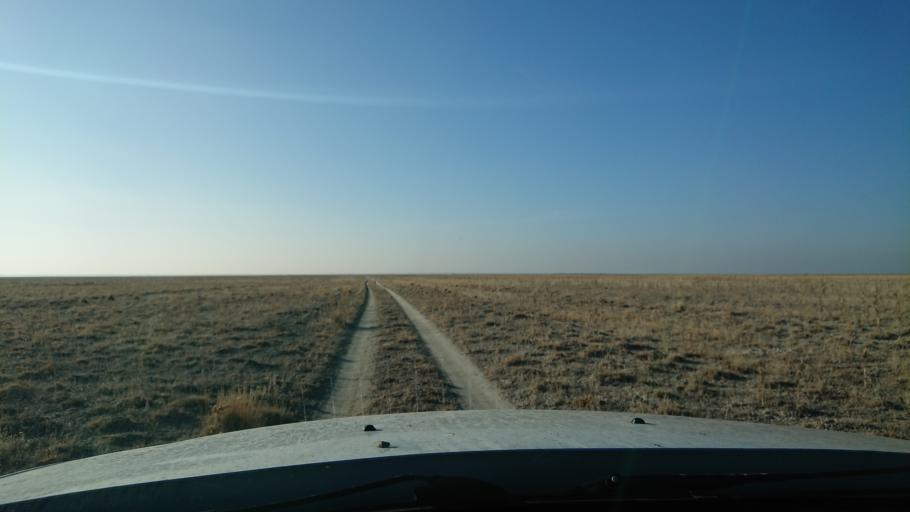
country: TR
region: Aksaray
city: Sultanhani
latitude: 38.3711
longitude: 33.5561
